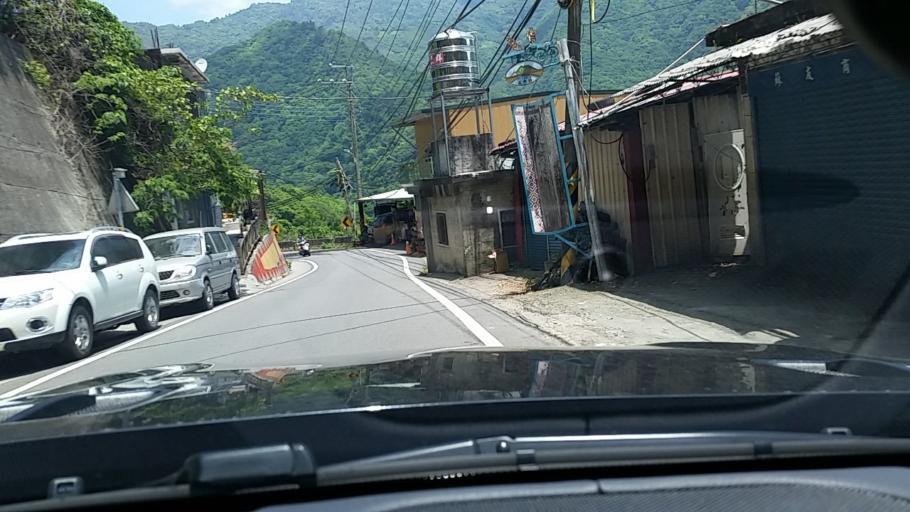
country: TW
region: Taiwan
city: Daxi
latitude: 24.6933
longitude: 121.3741
